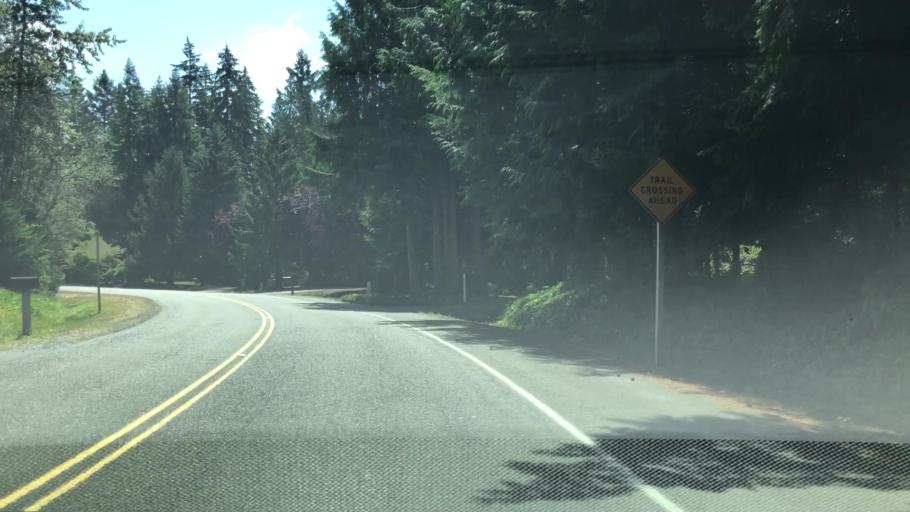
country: US
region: Washington
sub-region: King County
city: Cottage Lake
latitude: 47.7342
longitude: -122.0847
